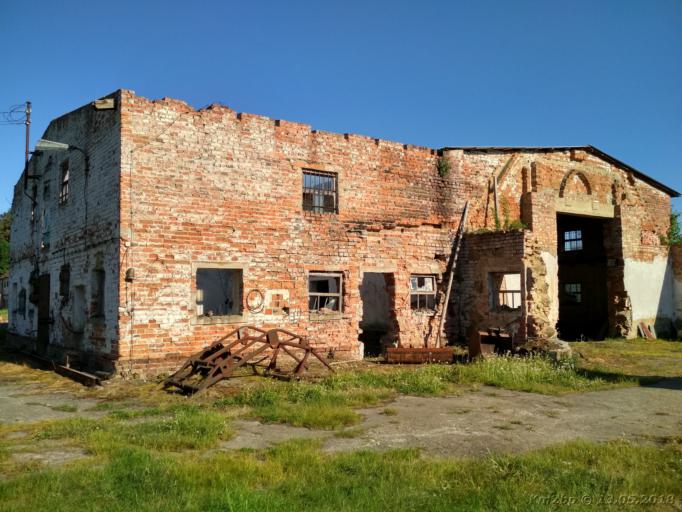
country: PL
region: Lubusz
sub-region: Powiat zielonogorski
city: Swidnica
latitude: 51.8856
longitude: 15.3645
